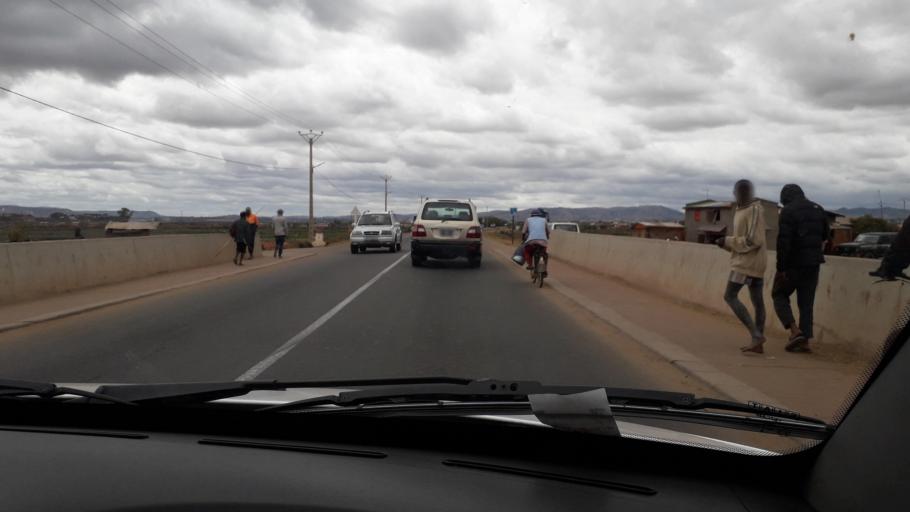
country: MG
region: Analamanga
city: Antananarivo
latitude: -18.8523
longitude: 47.5122
